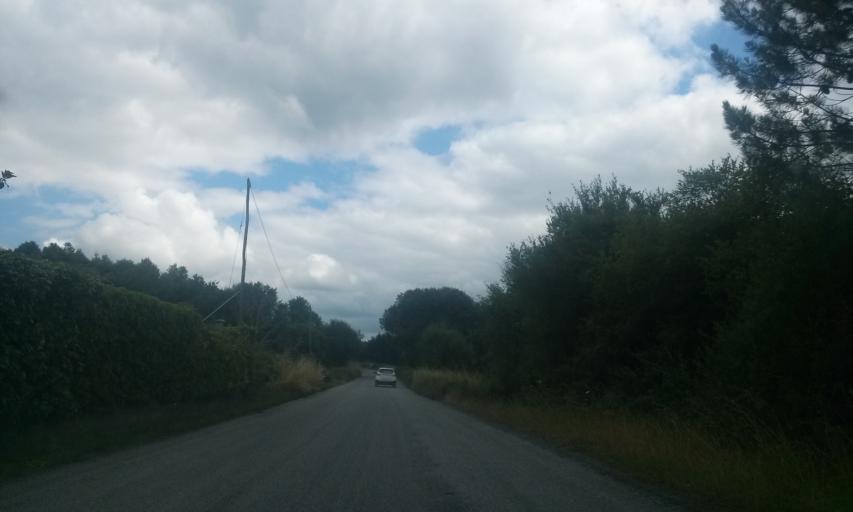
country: ES
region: Galicia
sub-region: Provincia de Lugo
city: Outeiro de Rei
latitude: 43.0633
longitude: -7.6156
